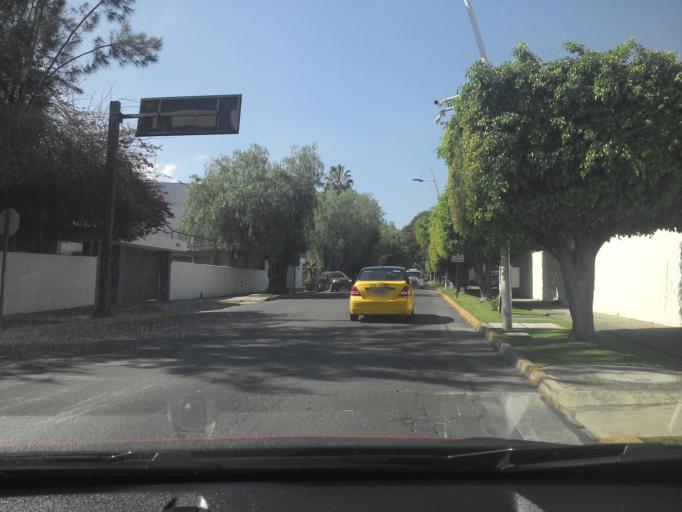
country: MX
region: Jalisco
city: Zapopan2
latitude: 20.6954
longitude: -103.3978
